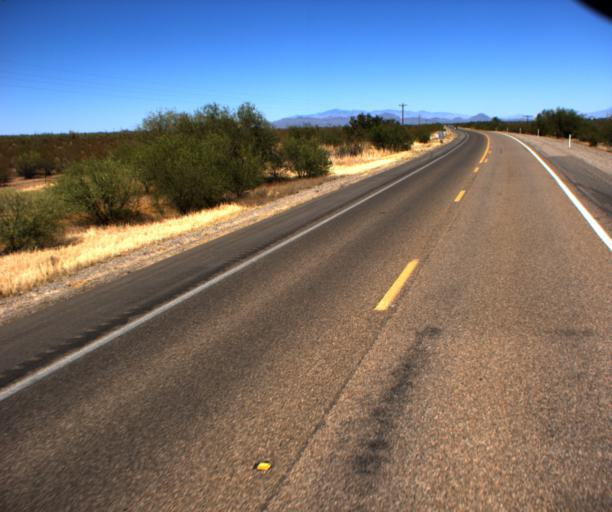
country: US
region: Arizona
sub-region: Pima County
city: Three Points
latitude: 32.0667
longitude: -111.3662
